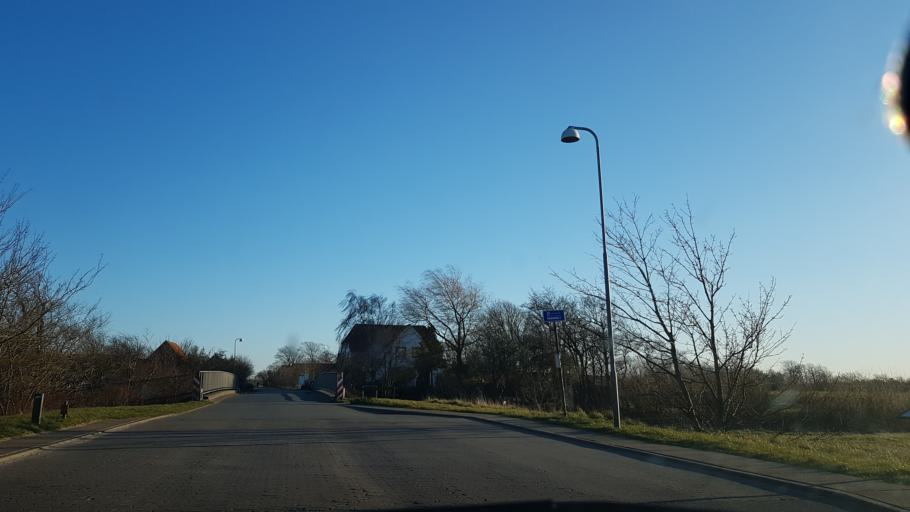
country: DK
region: South Denmark
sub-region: Esbjerg Kommune
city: Bramming
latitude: 55.3957
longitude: 8.7135
